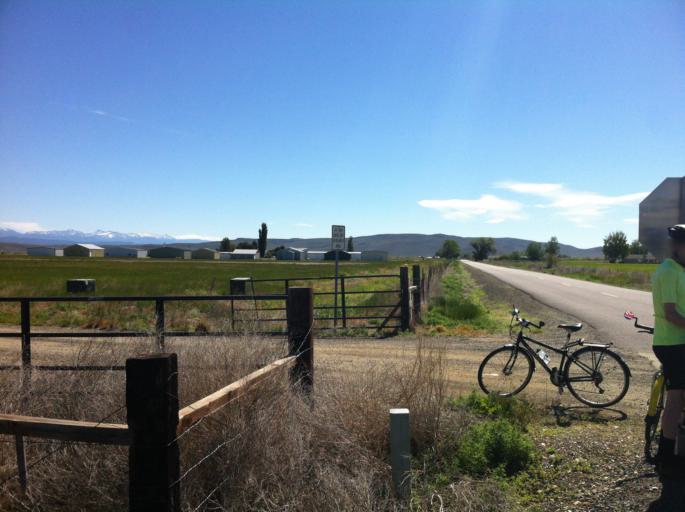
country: US
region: Oregon
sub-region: Baker County
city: Baker City
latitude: 44.8326
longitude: -117.8153
